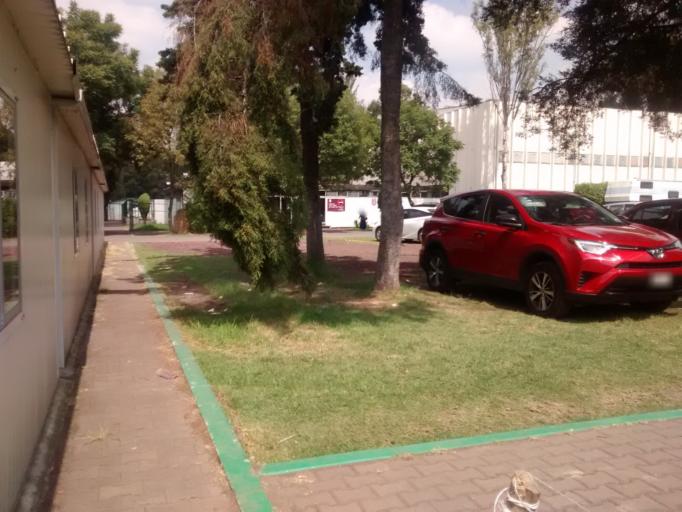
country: MX
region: Mexico City
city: Coyoacan
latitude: 19.3301
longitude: -99.1122
